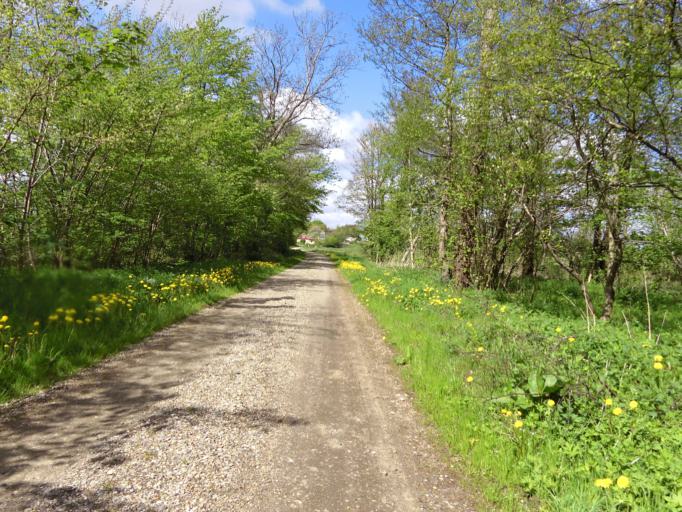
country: DK
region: South Denmark
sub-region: Haderslev Kommune
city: Gram
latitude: 55.3257
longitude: 9.0606
